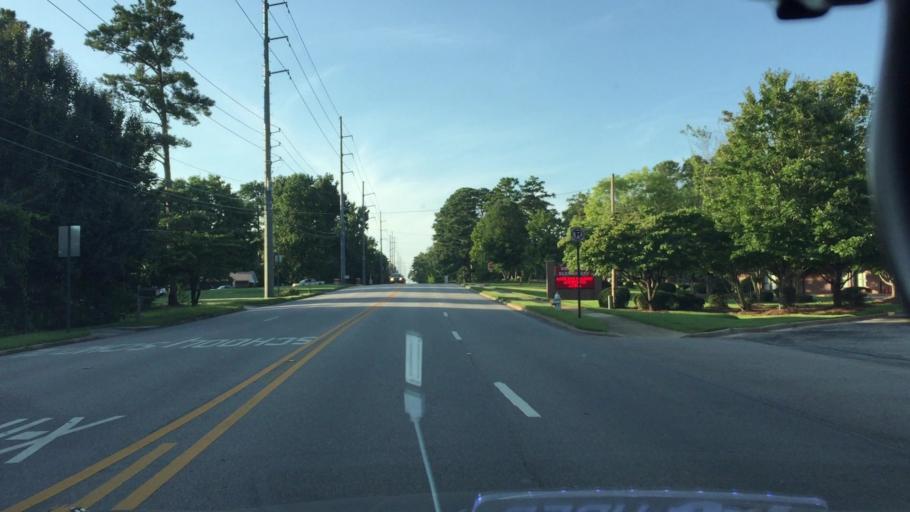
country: US
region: Alabama
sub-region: Lee County
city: Auburn
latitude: 32.5997
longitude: -85.4648
